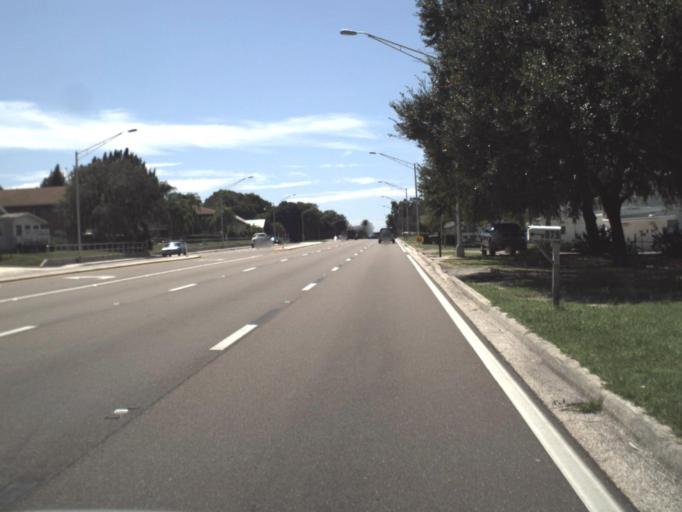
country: US
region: Florida
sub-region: Polk County
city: Lake Alfred
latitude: 28.0832
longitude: -81.7300
